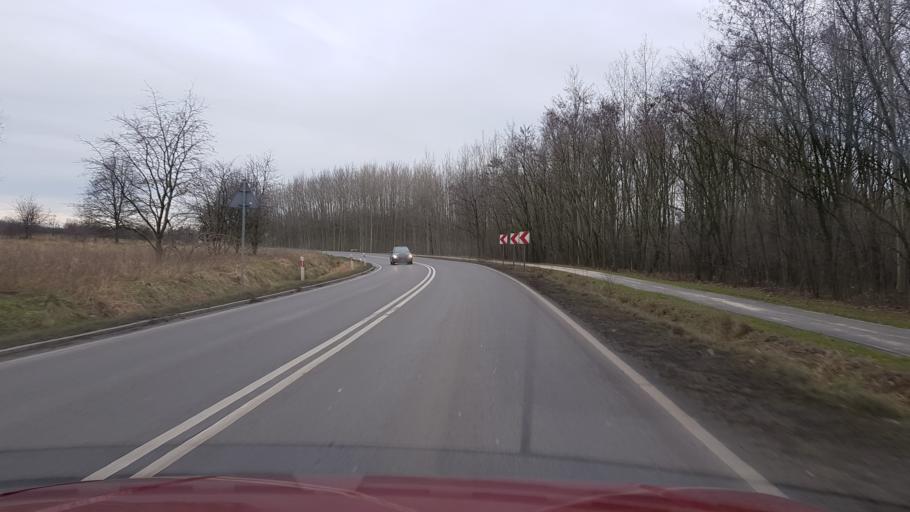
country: PL
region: West Pomeranian Voivodeship
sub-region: Powiat policki
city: Police
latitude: 53.5852
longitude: 14.5514
